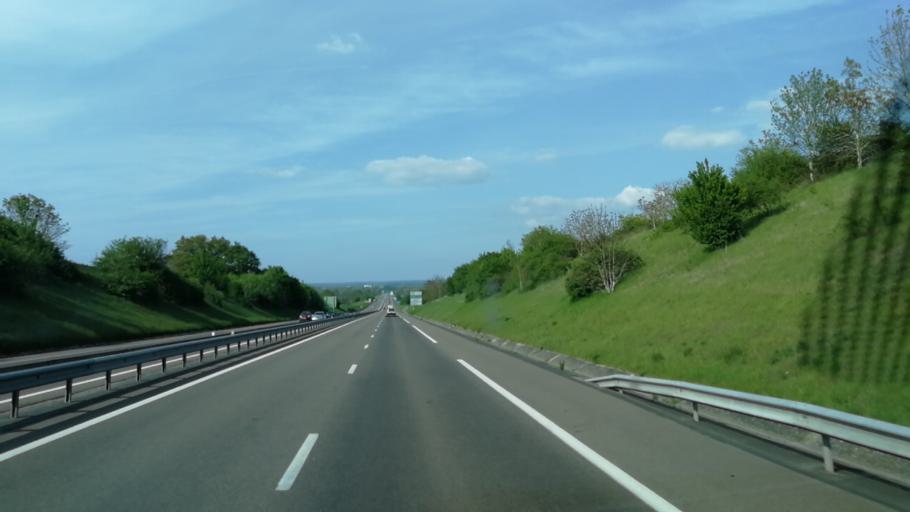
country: FR
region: Bourgogne
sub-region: Departement de la Nievre
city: Challuy
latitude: 46.9439
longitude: 3.1625
